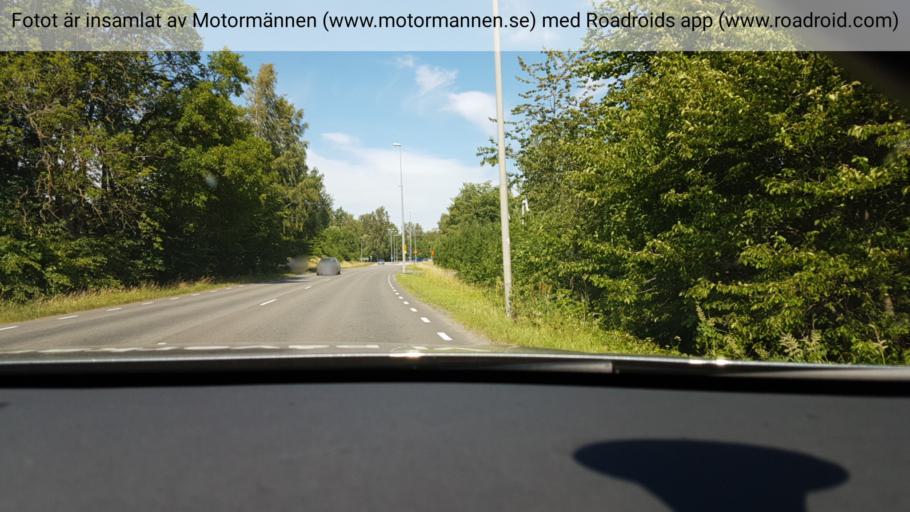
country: SE
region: Vaestra Goetaland
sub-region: Skovde Kommun
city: Skoevde
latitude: 58.4207
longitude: 13.8463
